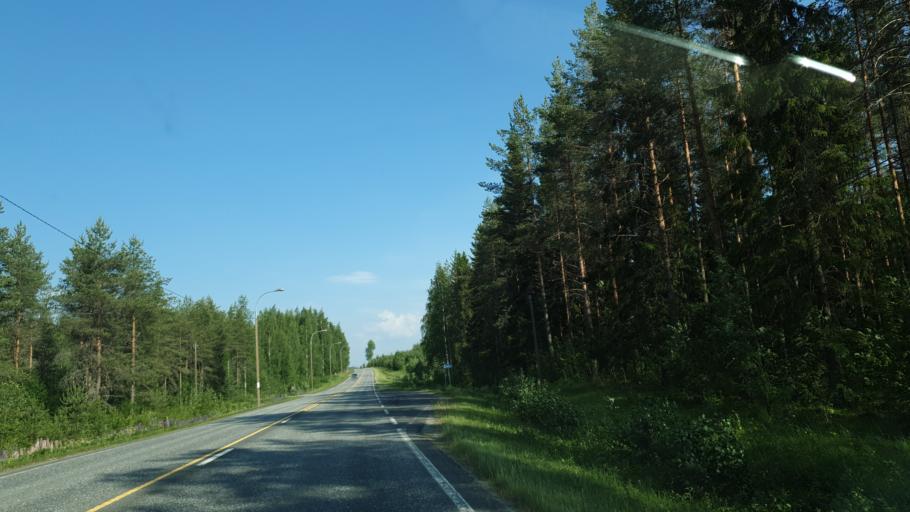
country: FI
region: Northern Savo
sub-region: Kuopio
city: Nilsiae
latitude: 63.1441
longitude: 27.8899
